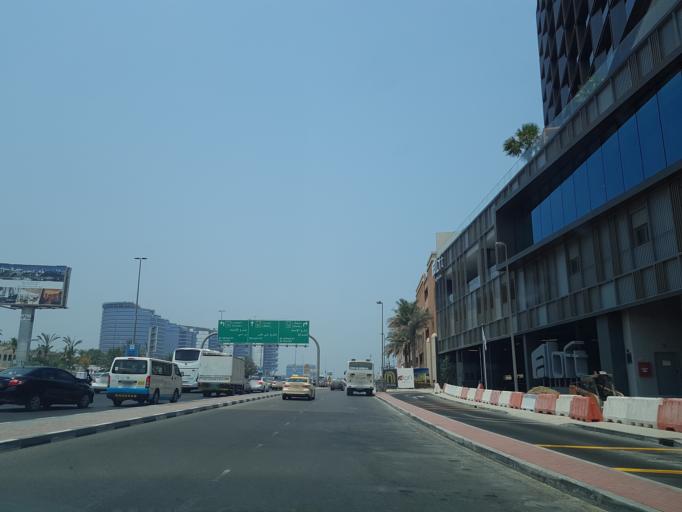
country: AE
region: Ash Shariqah
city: Sharjah
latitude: 25.2505
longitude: 55.3324
